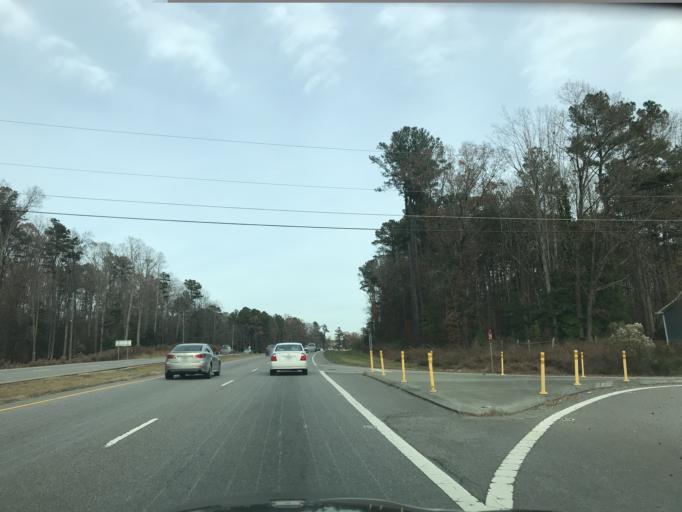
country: US
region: North Carolina
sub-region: Wake County
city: Rolesville
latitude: 35.8882
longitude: -78.5232
